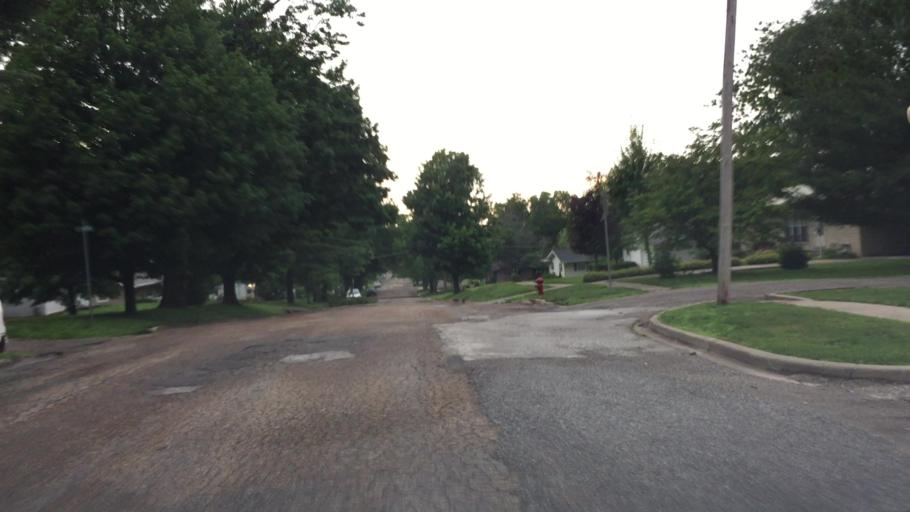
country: US
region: Illinois
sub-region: Hancock County
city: Warsaw
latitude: 40.3560
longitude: -91.4301
